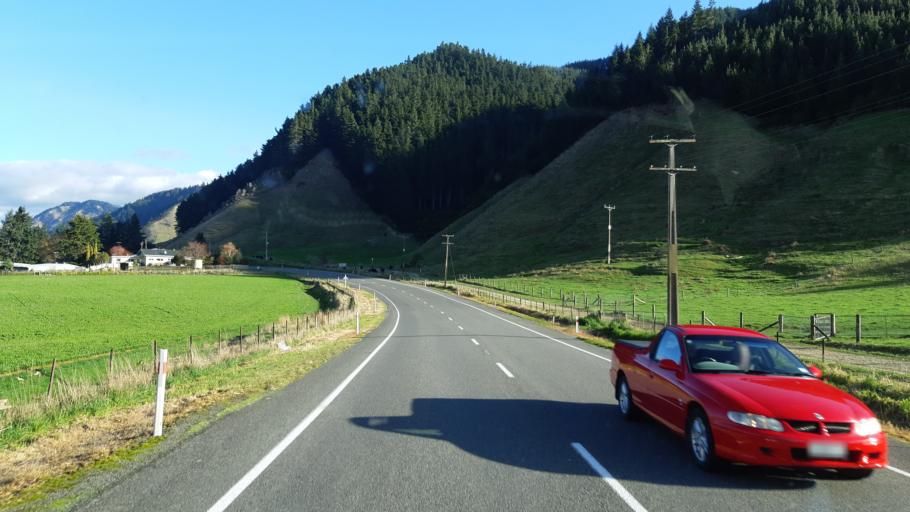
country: NZ
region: Marlborough
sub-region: Marlborough District
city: Picton
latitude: -41.3051
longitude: 173.7690
